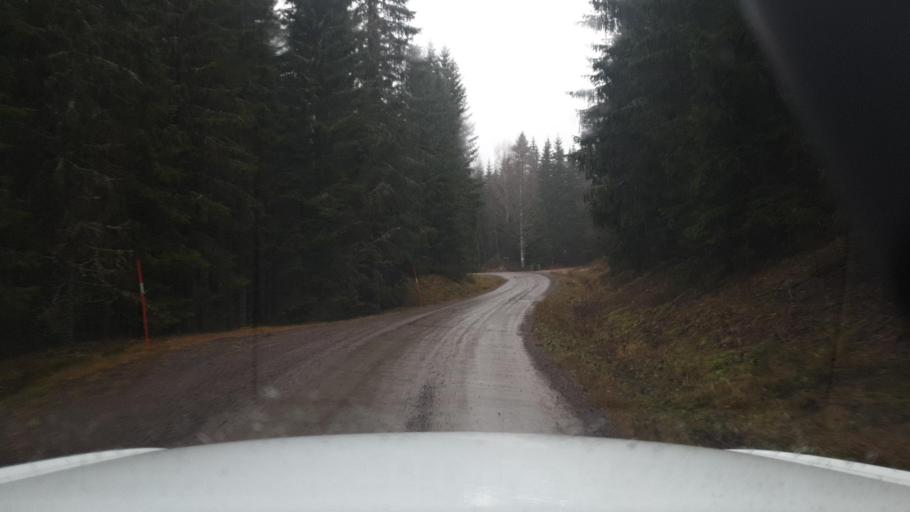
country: SE
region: Vaermland
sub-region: Sunne Kommun
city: Sunne
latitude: 59.8615
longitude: 12.8750
